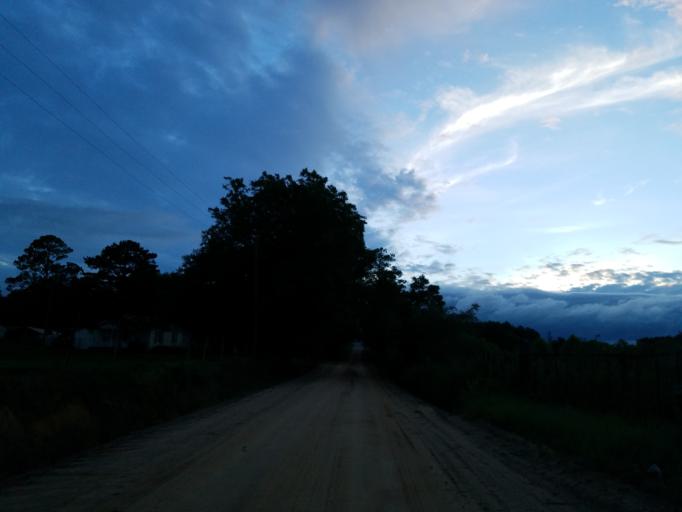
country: US
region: Georgia
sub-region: Tift County
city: Tifton
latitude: 31.5315
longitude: -83.5188
